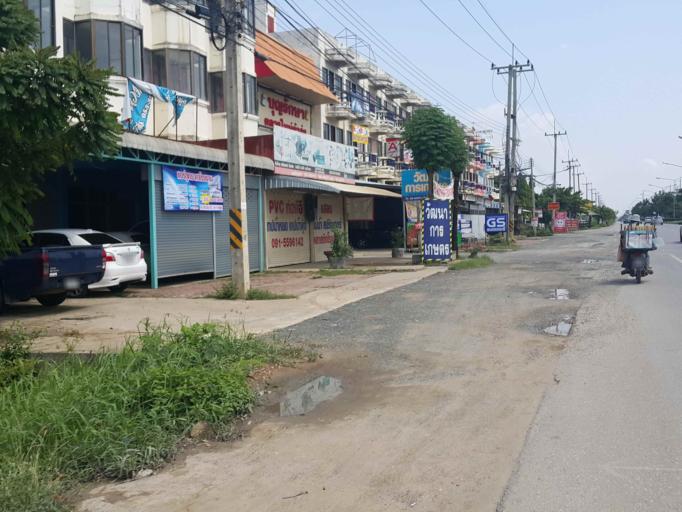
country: TH
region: Chiang Mai
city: San Sai
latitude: 18.8709
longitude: 99.0156
